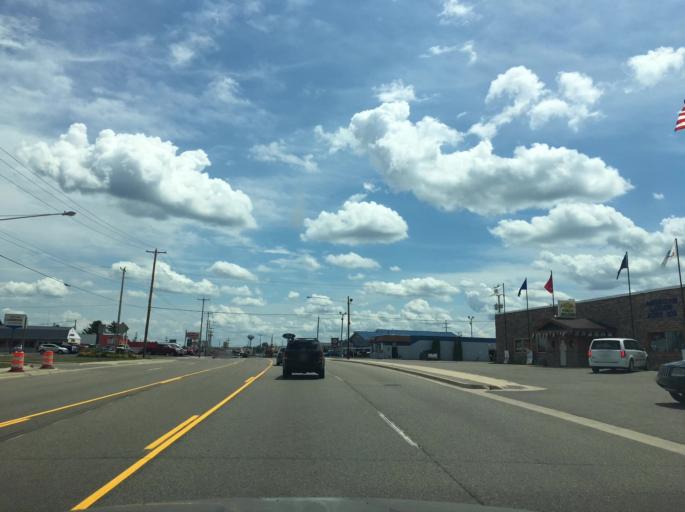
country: US
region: Michigan
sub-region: Crawford County
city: Grayling
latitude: 44.6591
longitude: -84.7118
